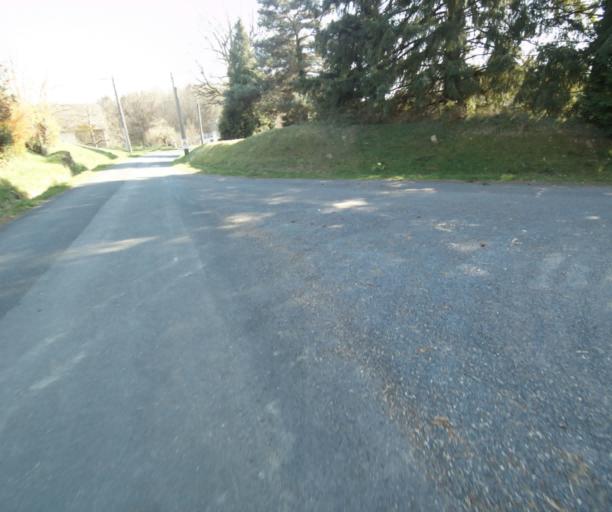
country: FR
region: Limousin
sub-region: Departement de la Correze
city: Saint-Mexant
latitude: 45.3247
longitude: 1.6253
